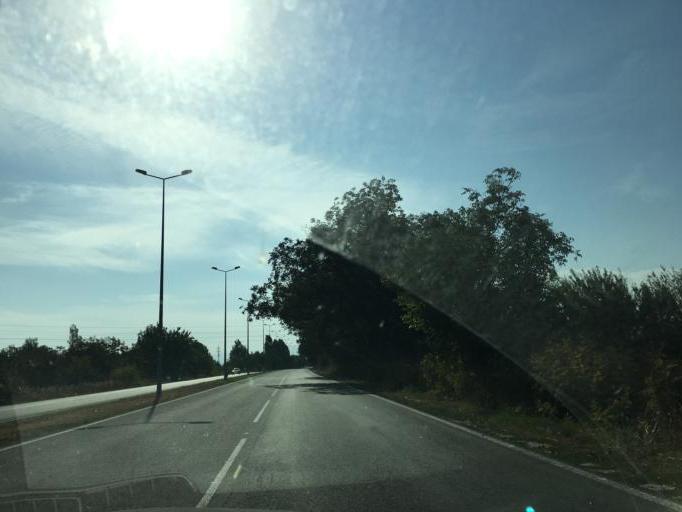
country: BG
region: Pazardzhik
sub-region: Obshtina Pazardzhik
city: Pazardzhik
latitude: 42.2185
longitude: 24.3153
